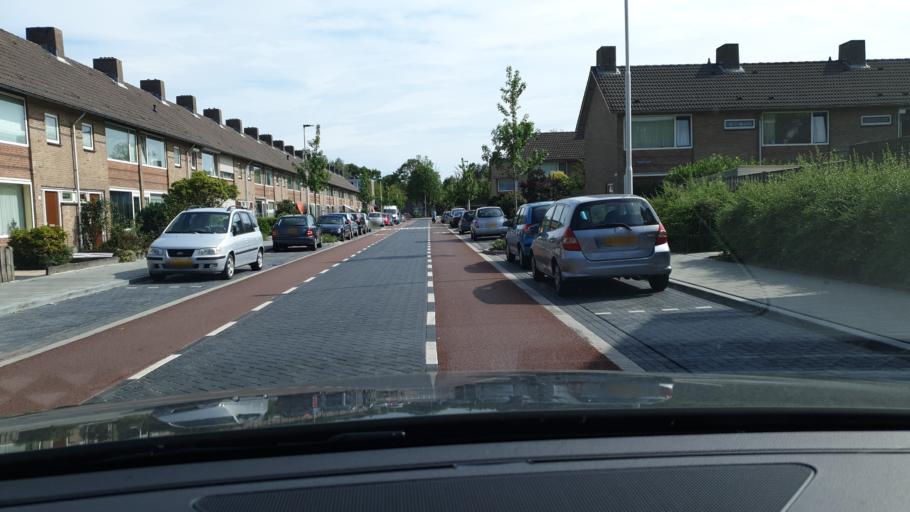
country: NL
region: North Brabant
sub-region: Gemeente Eindhoven
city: Eindhoven
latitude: 51.4762
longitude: 5.4666
